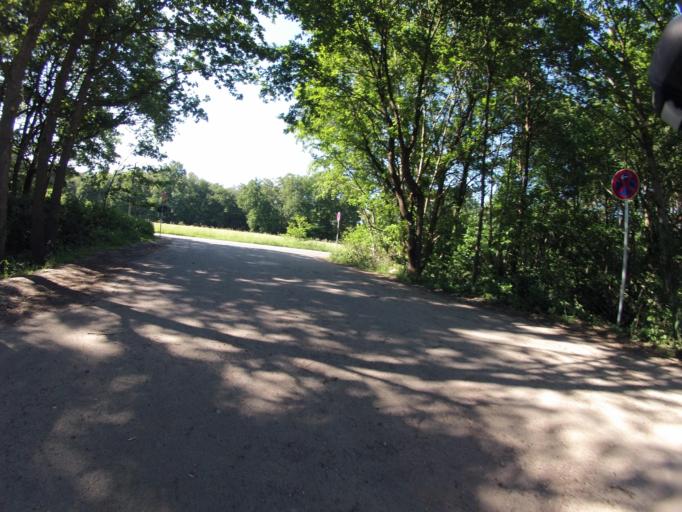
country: DE
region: North Rhine-Westphalia
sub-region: Regierungsbezirk Munster
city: Dreierwalde
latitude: 52.2639
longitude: 7.4767
